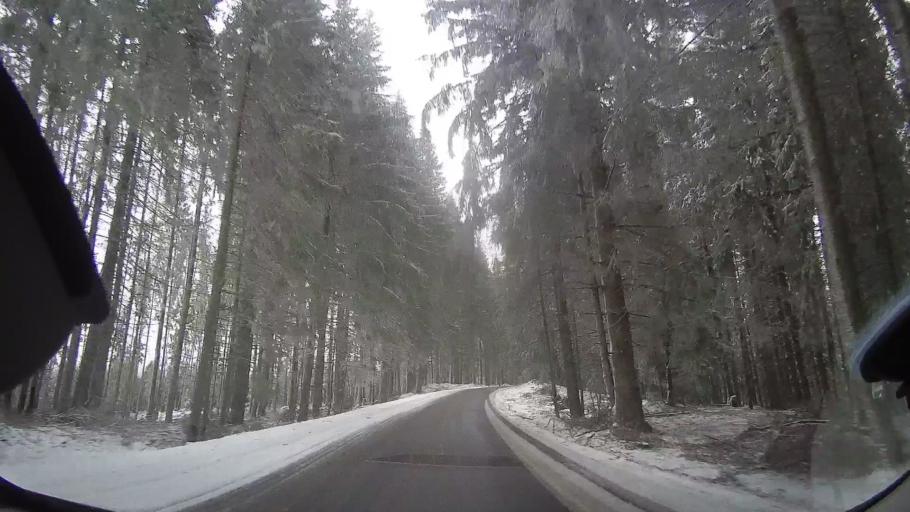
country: RO
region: Cluj
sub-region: Comuna Belis
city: Belis
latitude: 46.6473
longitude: 23.0437
